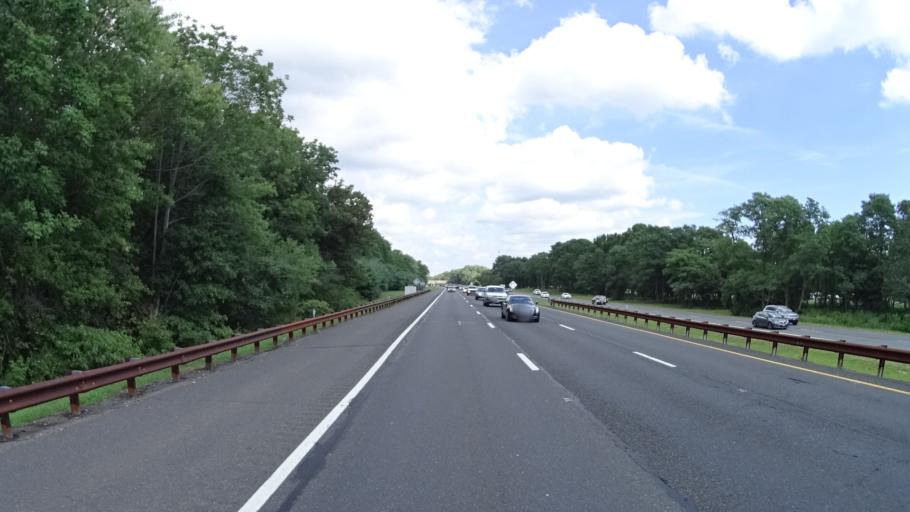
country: US
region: New Jersey
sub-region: Monmouth County
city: Tinton Falls
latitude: 40.3036
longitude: -74.0941
